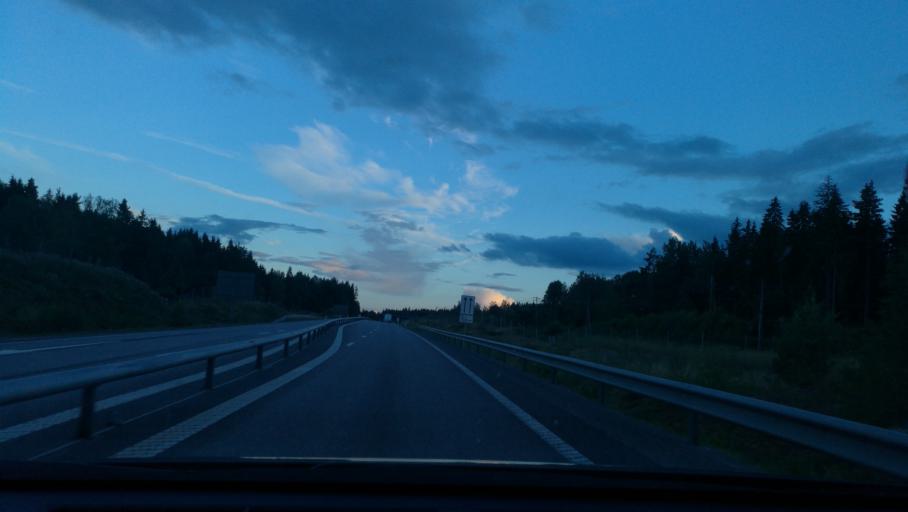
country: SE
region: Soedermanland
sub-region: Katrineholms Kommun
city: Katrineholm
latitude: 58.9305
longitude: 16.1960
